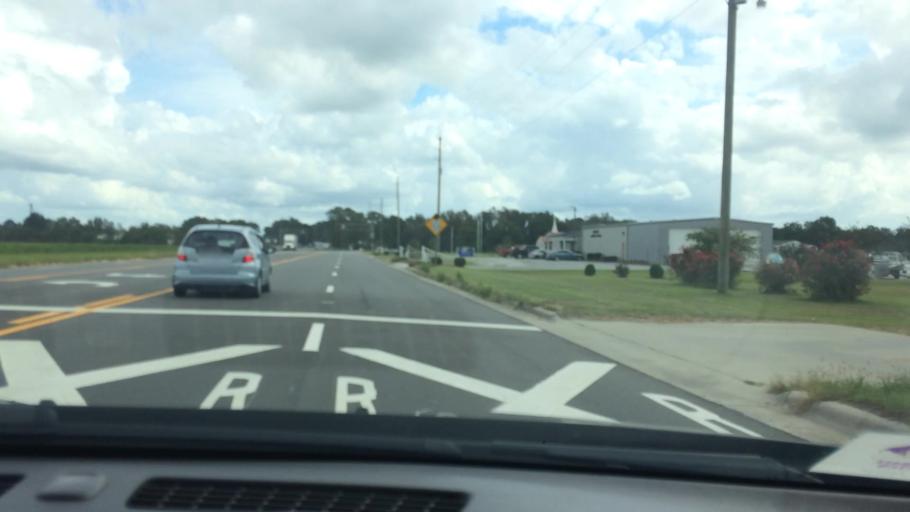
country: US
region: North Carolina
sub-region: Pitt County
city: Farmville
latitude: 35.5936
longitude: -77.6254
